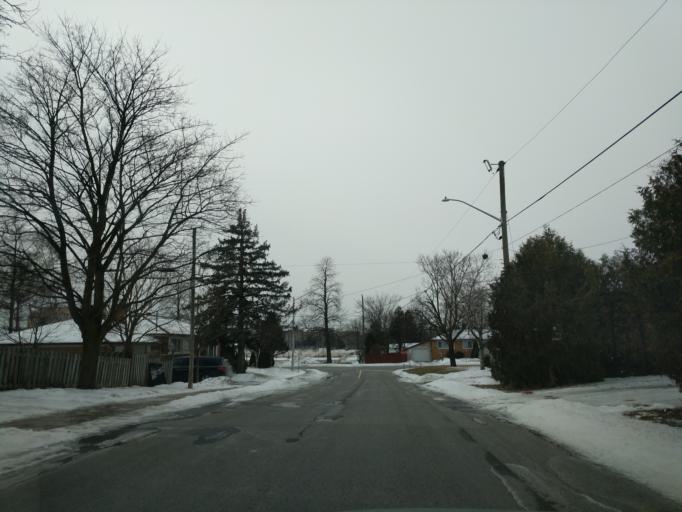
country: CA
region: Ontario
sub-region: York
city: Richmond Hill
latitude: 43.8767
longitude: -79.4210
